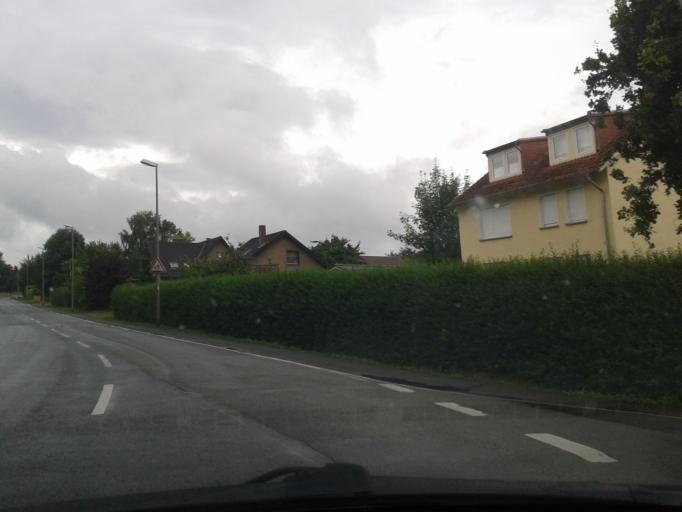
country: DE
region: North Rhine-Westphalia
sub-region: Regierungsbezirk Detmold
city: Lemgo
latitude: 51.9822
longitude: 8.8944
